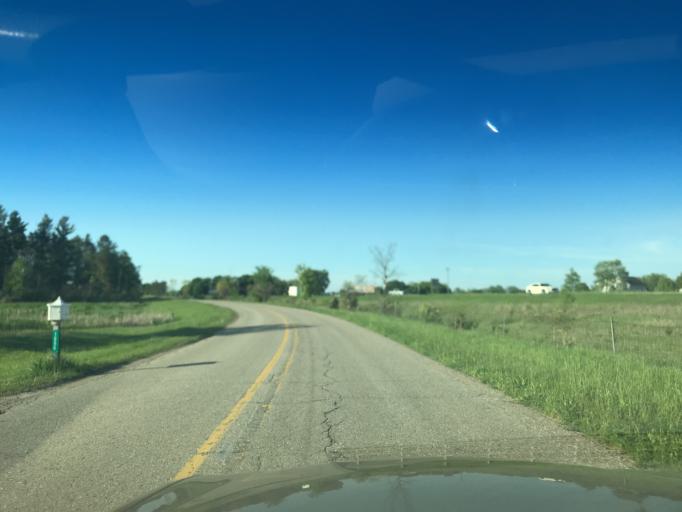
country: US
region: Michigan
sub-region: Ingham County
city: Mason
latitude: 42.5268
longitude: -84.4446
